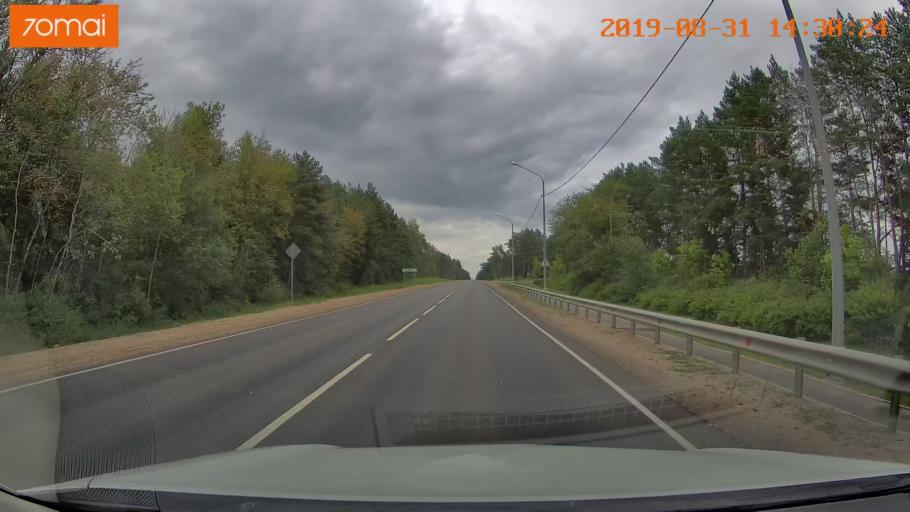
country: RU
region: Smolensk
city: Yekimovichi
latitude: 54.1313
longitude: 33.3500
